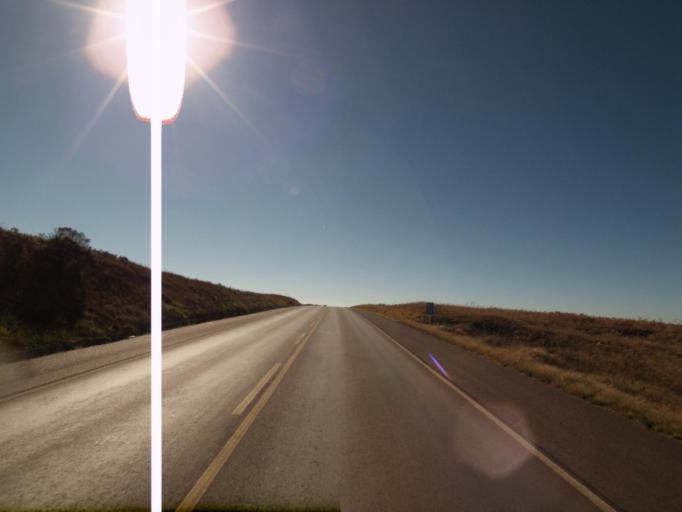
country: BR
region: Parana
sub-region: Palmas
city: Palmas
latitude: -26.7202
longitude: -51.6223
